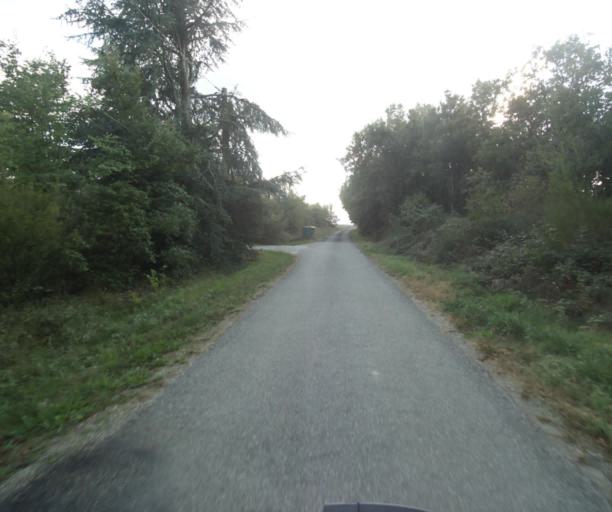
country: FR
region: Midi-Pyrenees
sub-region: Departement de la Haute-Garonne
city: Launac
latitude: 43.8121
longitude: 1.1311
